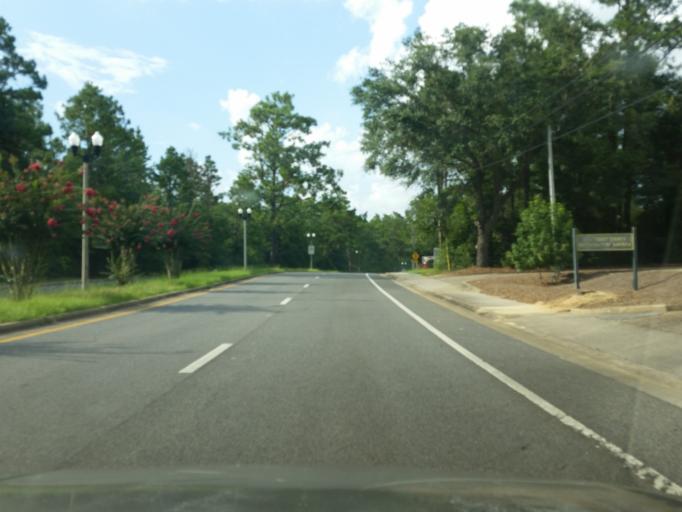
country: US
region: Florida
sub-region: Escambia County
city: Ferry Pass
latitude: 30.5353
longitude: -87.2210
